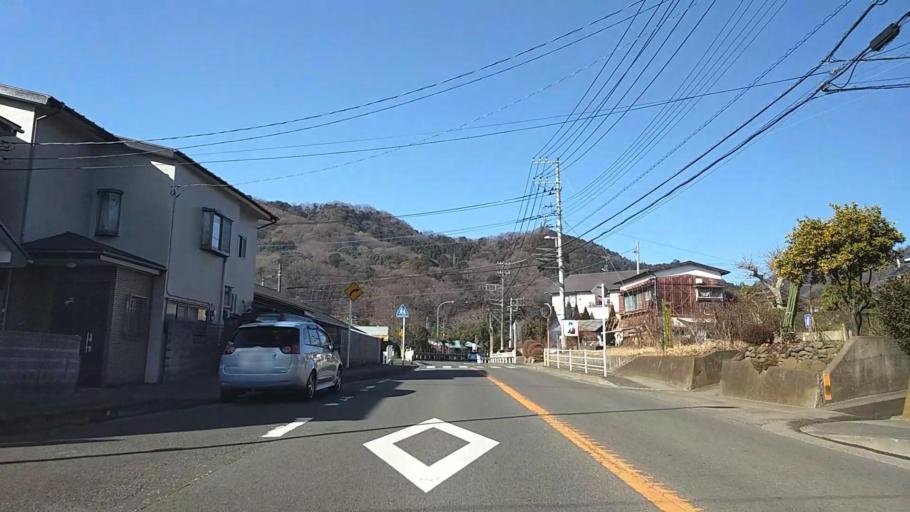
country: JP
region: Kanagawa
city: Atsugi
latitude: 35.4753
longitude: 139.3094
